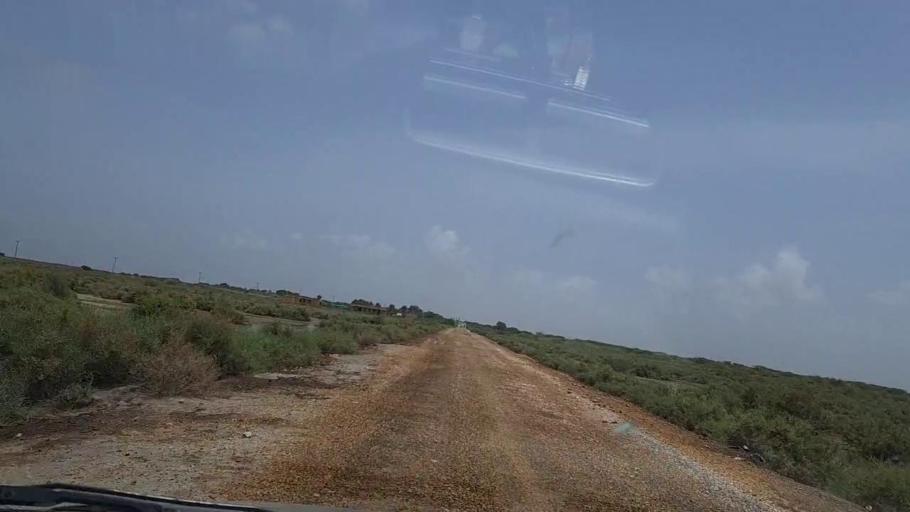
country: PK
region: Sindh
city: Keti Bandar
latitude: 24.1531
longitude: 67.5307
